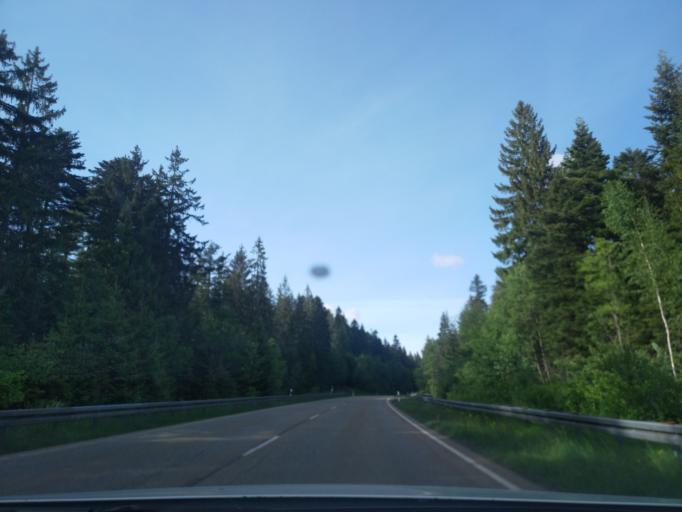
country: DE
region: Baden-Wuerttemberg
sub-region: Karlsruhe Region
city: Freudenstadt
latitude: 48.4888
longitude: 8.4135
